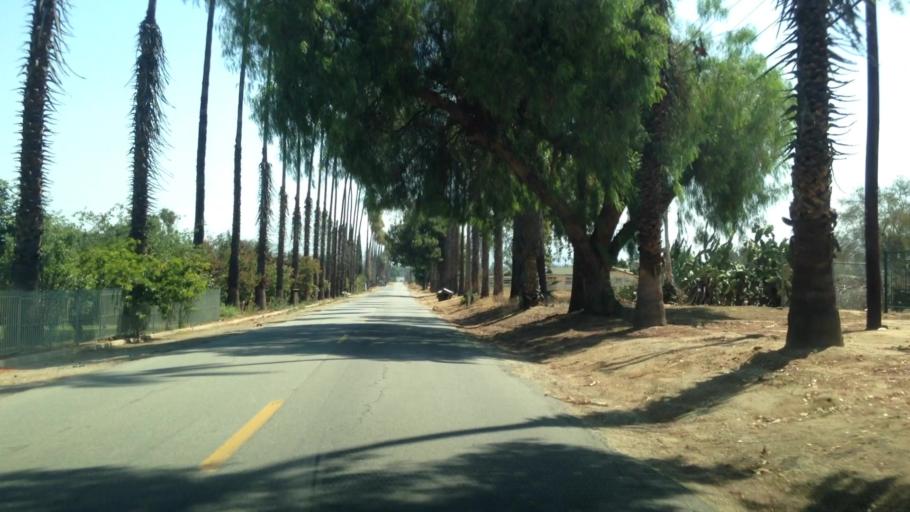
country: US
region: California
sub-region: Riverside County
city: Riverside
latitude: 33.8921
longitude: -117.4394
